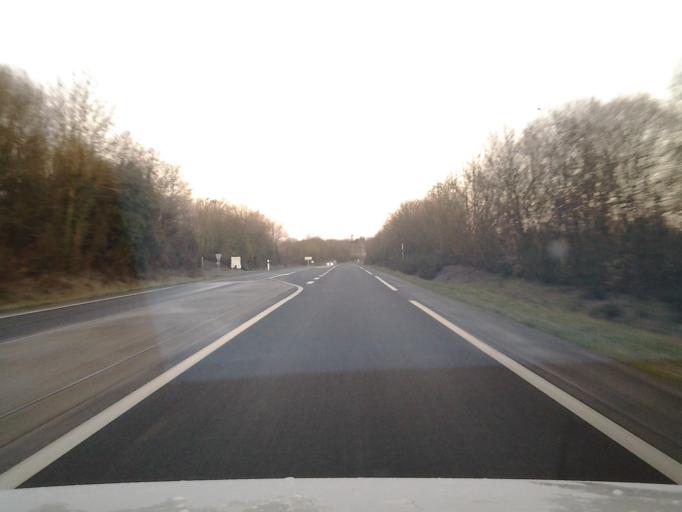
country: FR
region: Pays de la Loire
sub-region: Departement de la Vendee
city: Les Epesses
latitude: 46.8913
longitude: -0.9219
